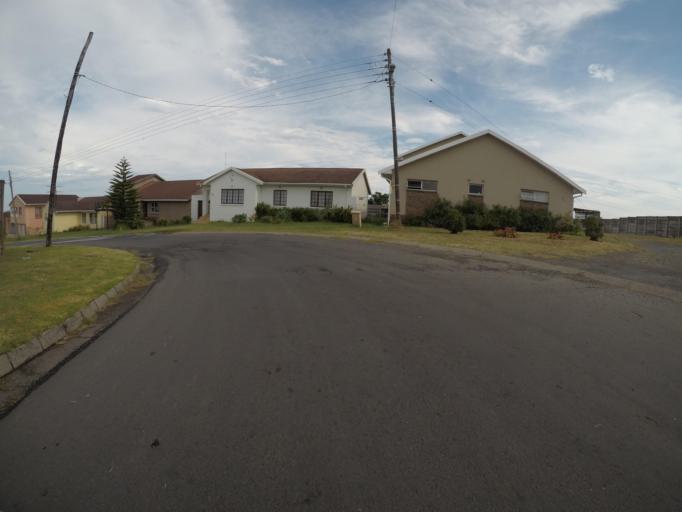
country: ZA
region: Eastern Cape
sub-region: Buffalo City Metropolitan Municipality
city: East London
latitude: -33.0239
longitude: 27.8737
